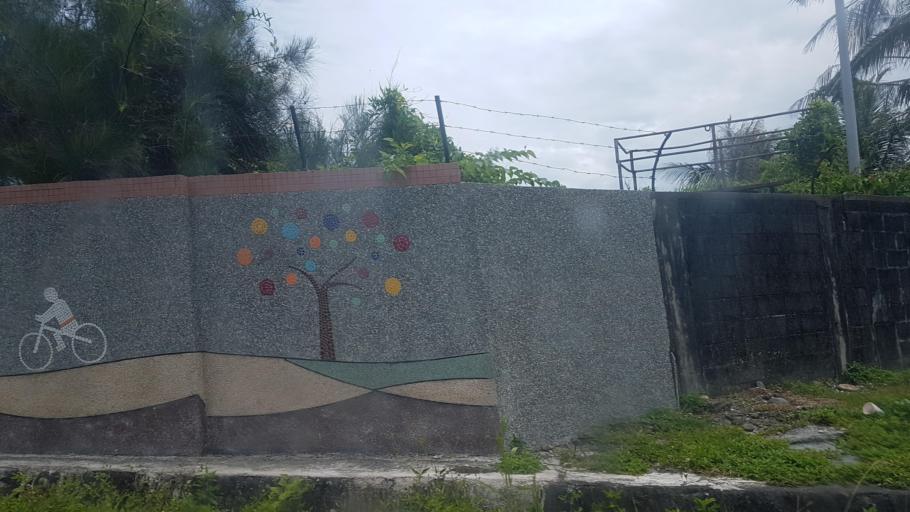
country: TW
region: Taiwan
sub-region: Hualien
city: Hualian
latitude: 24.0016
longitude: 121.6412
